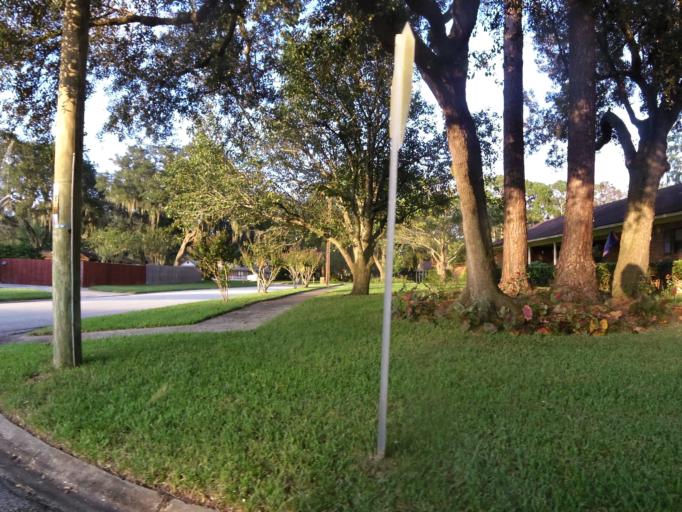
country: US
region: Florida
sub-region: Clay County
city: Orange Park
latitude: 30.2043
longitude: -81.6237
